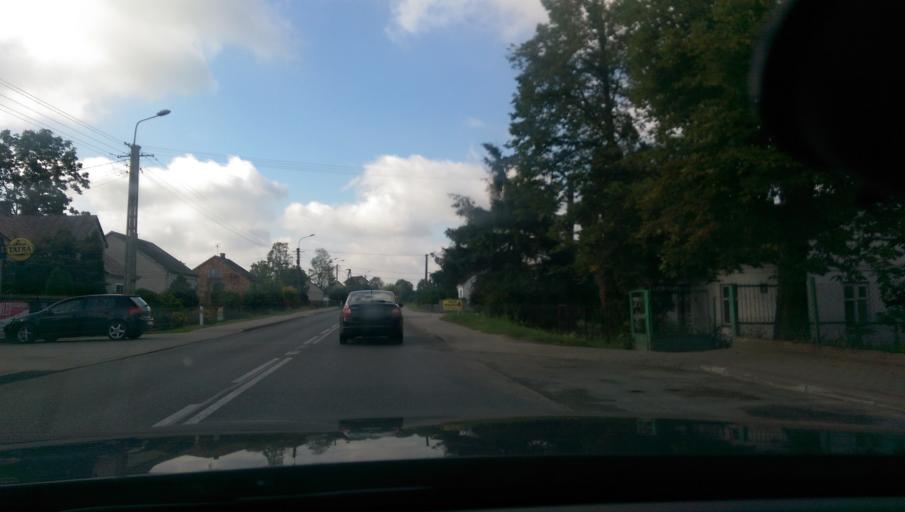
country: PL
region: Masovian Voivodeship
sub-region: Powiat ciechanowski
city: Ojrzen
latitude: 52.7646
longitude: 20.5430
